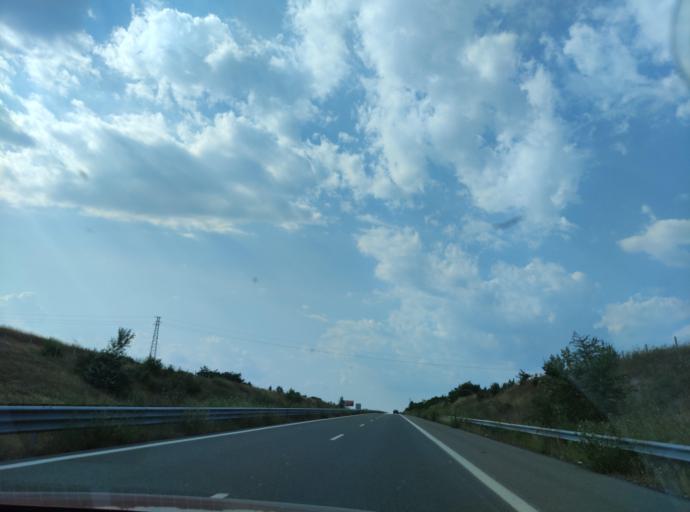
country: BG
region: Blagoevgrad
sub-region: Obshtina Sandanski
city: Sandanski
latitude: 41.4615
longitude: 23.3178
